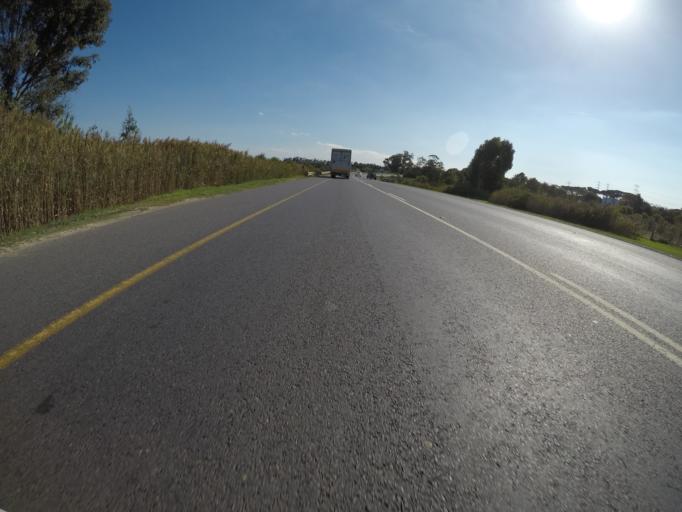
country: ZA
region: Western Cape
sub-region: City of Cape Town
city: Kraaifontein
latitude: -33.9024
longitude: 18.7223
